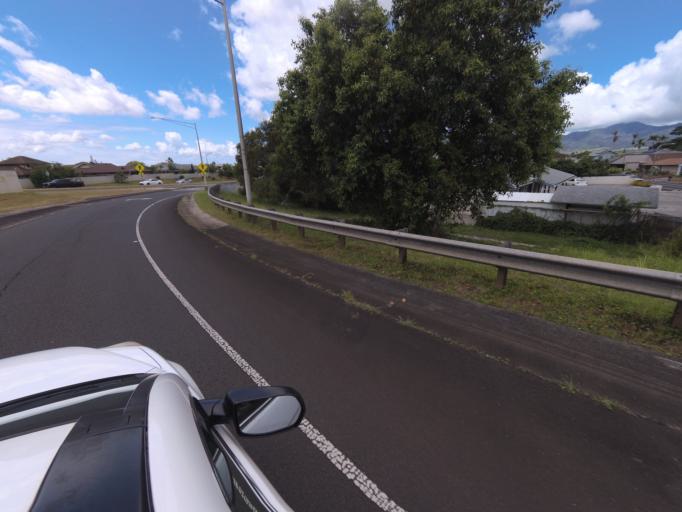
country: US
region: Hawaii
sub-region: Honolulu County
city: Waipi'o Acres
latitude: 21.4649
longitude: -158.0056
